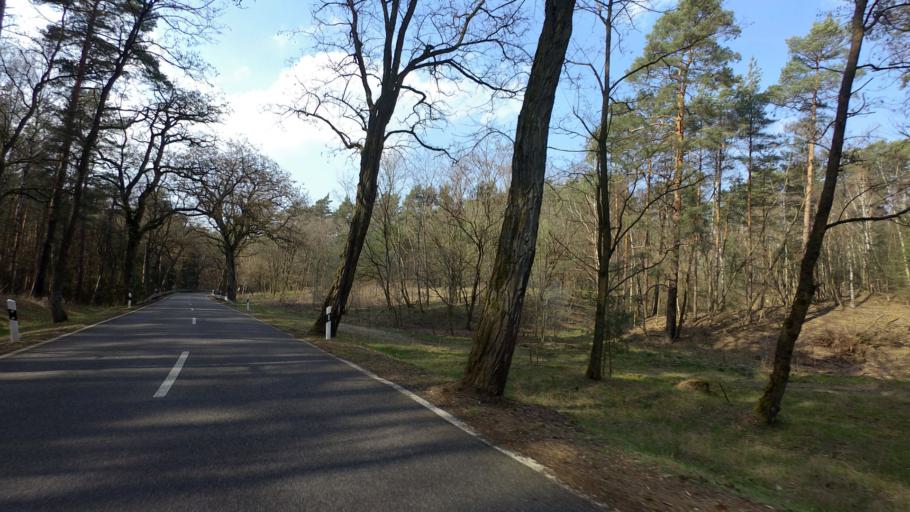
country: DE
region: Brandenburg
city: Dahme
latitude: 51.9342
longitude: 13.4494
